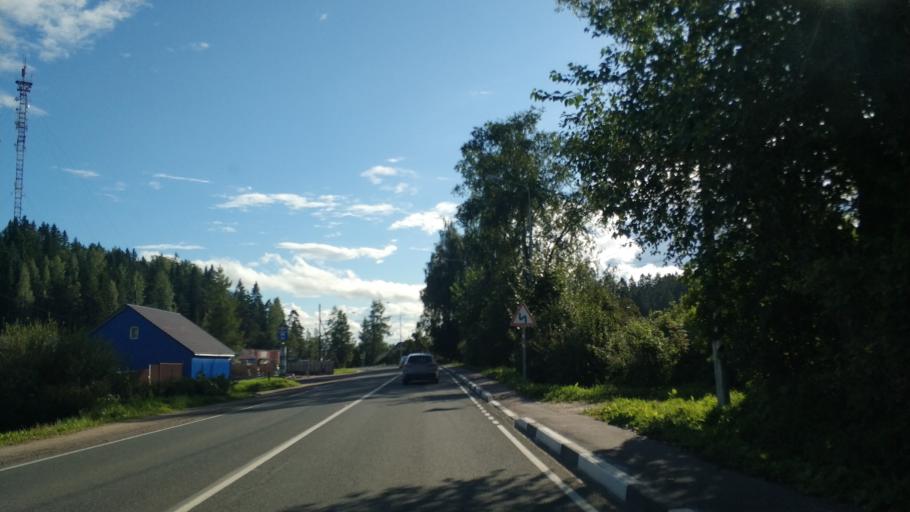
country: RU
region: Republic of Karelia
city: Lakhdenpokh'ya
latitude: 61.5271
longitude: 30.2026
